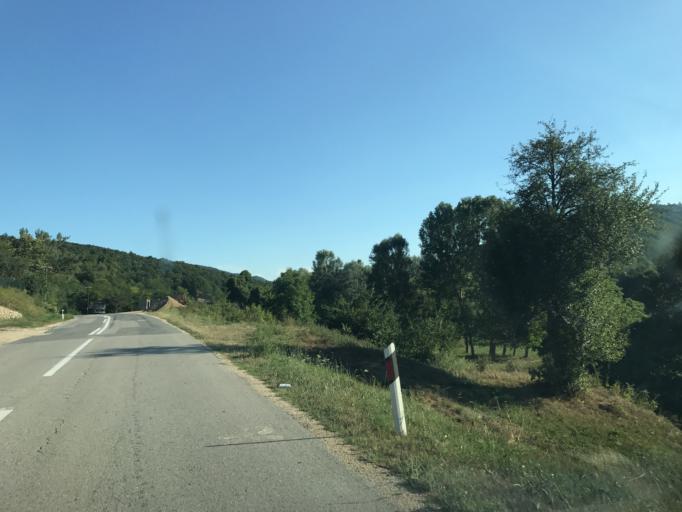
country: RO
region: Mehedinti
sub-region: Comuna Svinita
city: Svinita
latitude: 44.3582
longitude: 22.1803
